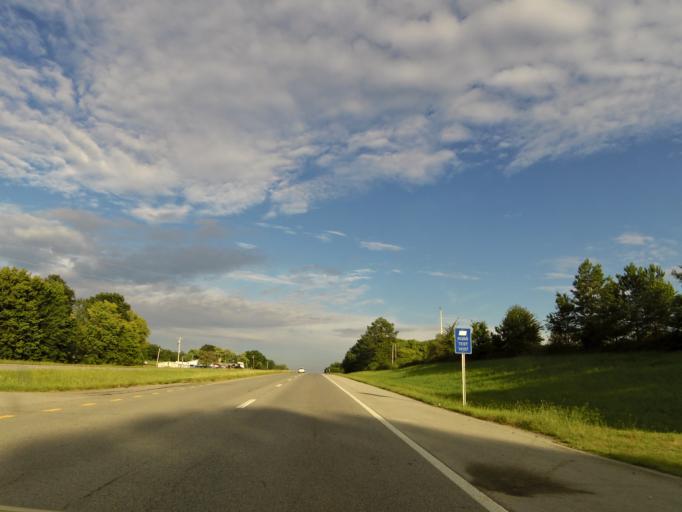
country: US
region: Alabama
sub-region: Lauderdale County
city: Rogersville
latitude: 34.8412
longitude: -87.3631
